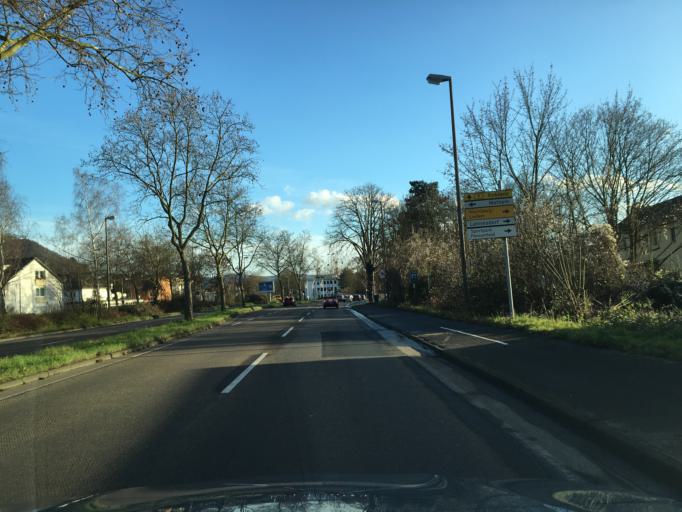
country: DE
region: North Rhine-Westphalia
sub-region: Regierungsbezirk Koln
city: Konigswinter
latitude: 50.6699
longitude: 7.1812
